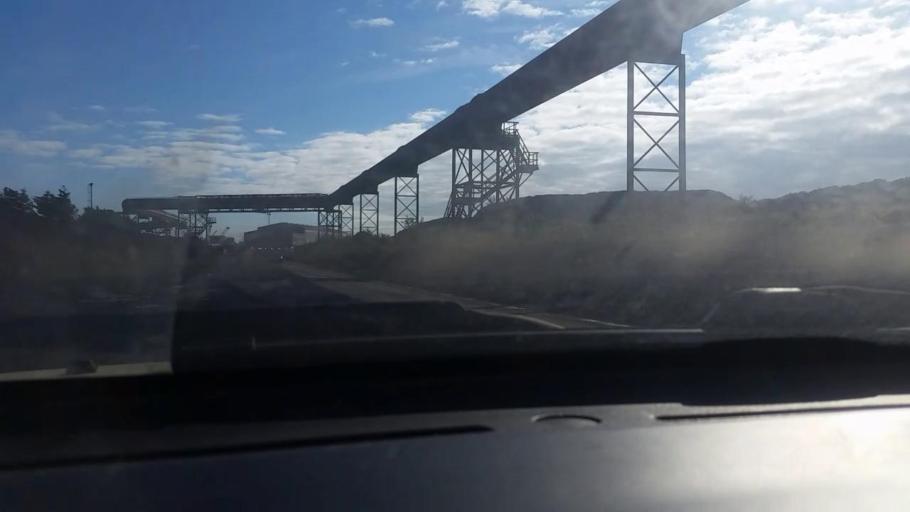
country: GB
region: Wales
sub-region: Neath Port Talbot
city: Taibach
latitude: 51.5731
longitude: -3.7790
